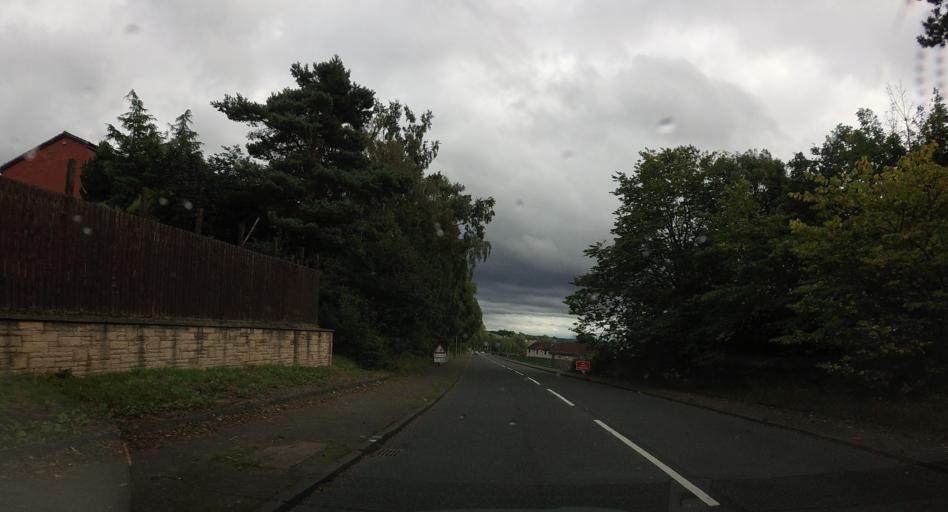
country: GB
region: Scotland
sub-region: Clackmannanshire
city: Alloa
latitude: 56.1319
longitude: -3.7940
